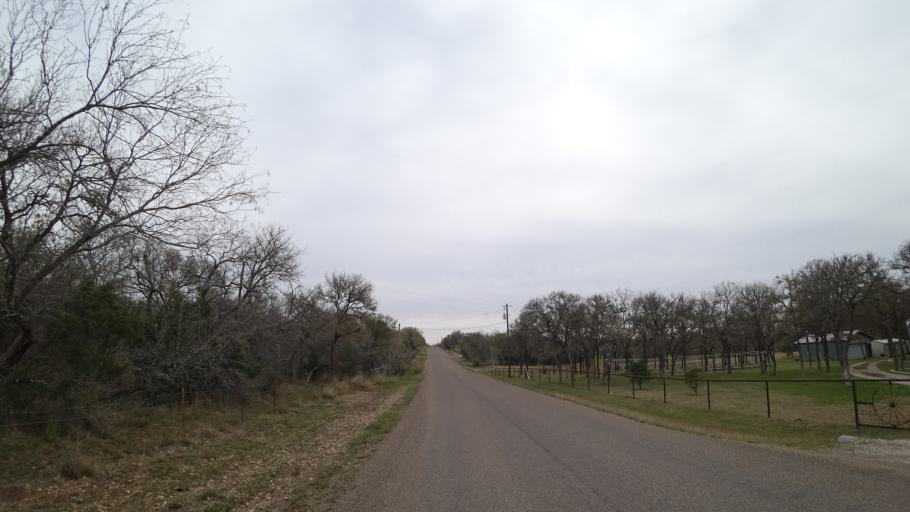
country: US
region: Texas
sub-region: Travis County
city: Garfield
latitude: 30.1094
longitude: -97.5625
